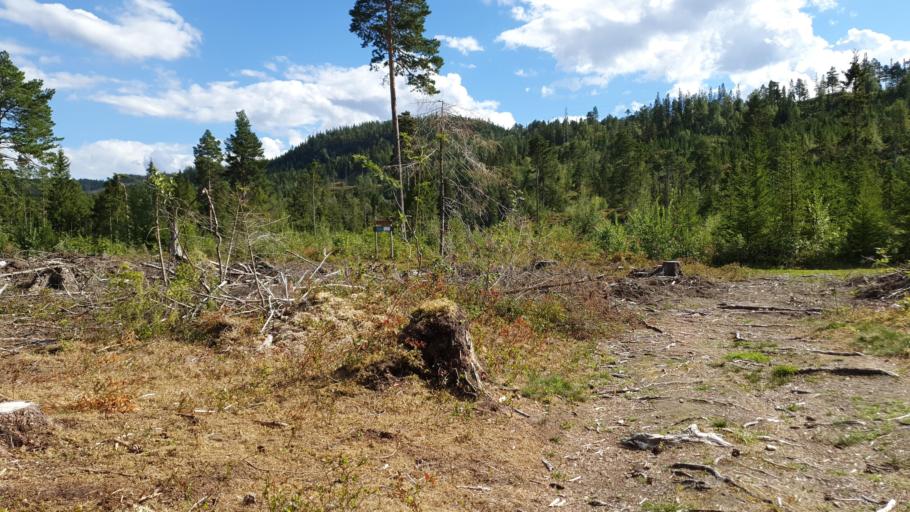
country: NO
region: Nord-Trondelag
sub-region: Levanger
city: Levanger
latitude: 63.6934
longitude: 11.2760
